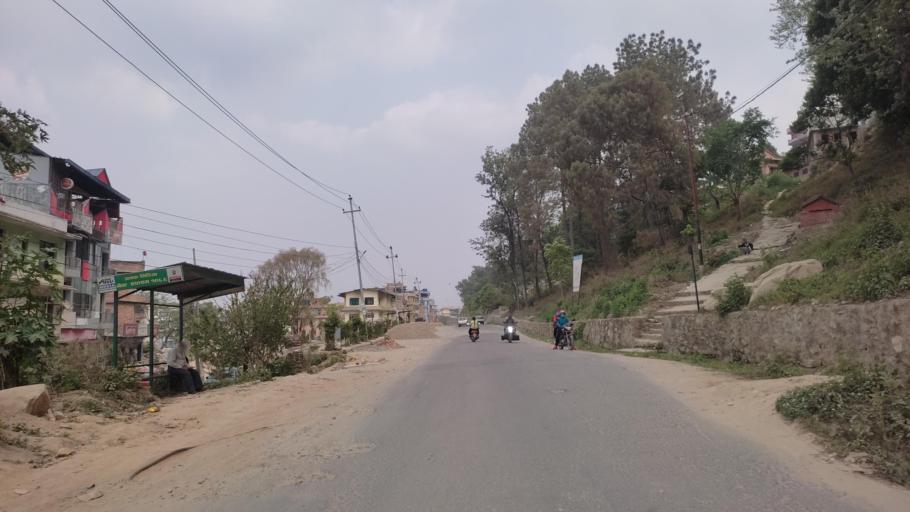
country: NP
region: Central Region
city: Kirtipur
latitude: 27.6813
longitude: 85.2754
